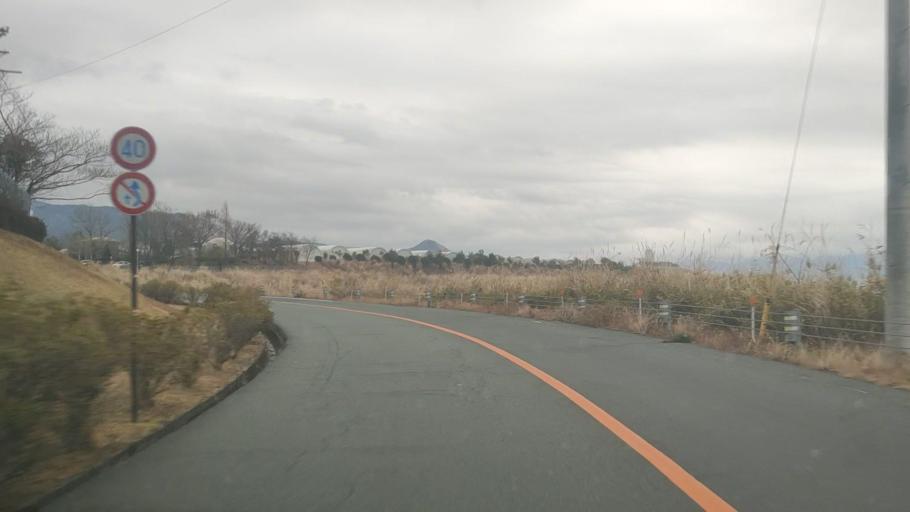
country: JP
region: Kumamoto
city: Aso
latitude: 32.8944
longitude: 131.0019
